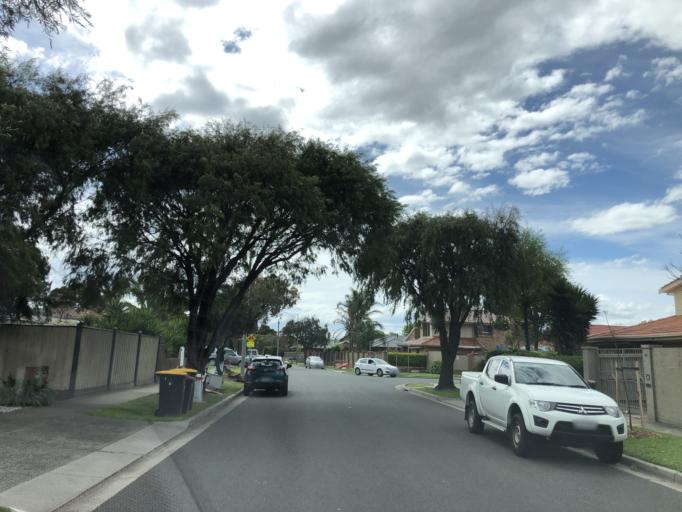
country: AU
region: Victoria
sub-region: Kingston
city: Carrum
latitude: -38.0764
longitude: 145.1350
